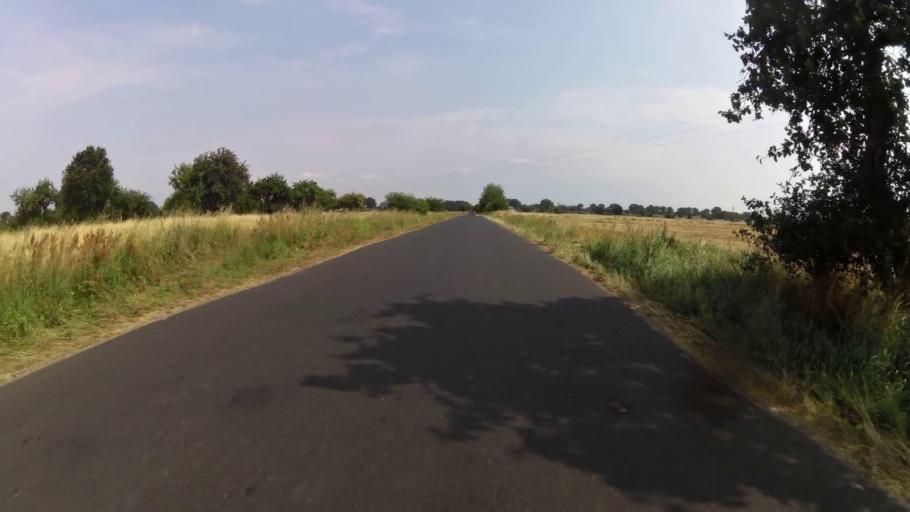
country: PL
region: West Pomeranian Voivodeship
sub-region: Powiat pyrzycki
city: Lipiany
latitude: 52.9686
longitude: 14.9944
